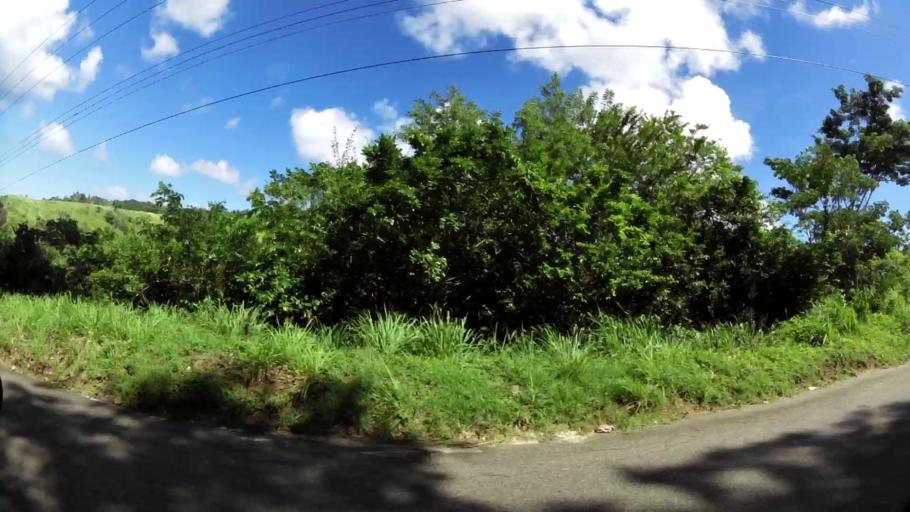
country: TT
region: Tobago
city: Scarborough
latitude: 11.1876
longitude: -60.7878
